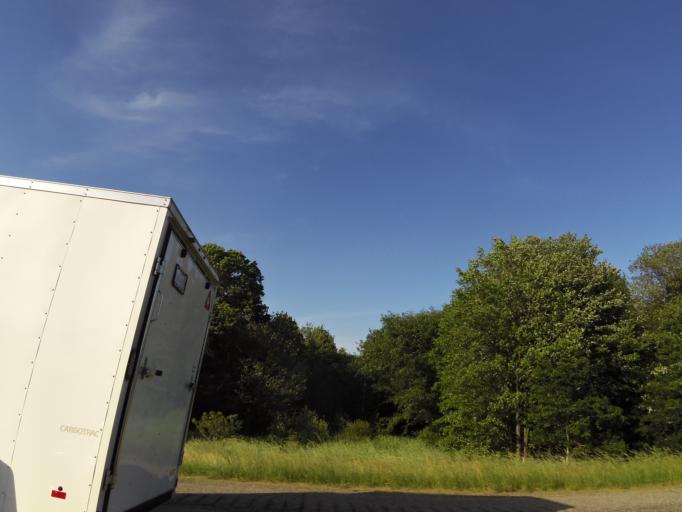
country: US
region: Wisconsin
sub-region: Columbia County
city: Wisconsin Dells
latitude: 43.6879
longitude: -89.8445
